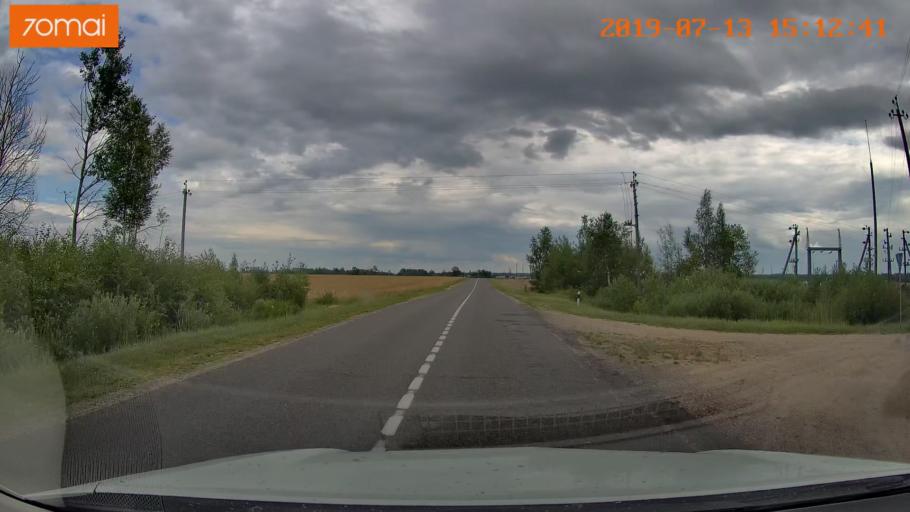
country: BY
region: Mogilev
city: Hlusha
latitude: 53.1461
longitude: 28.7955
